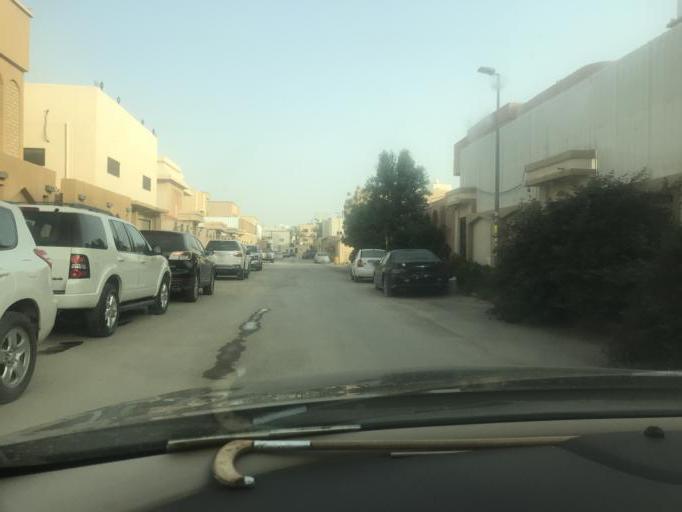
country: SA
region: Ar Riyad
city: Riyadh
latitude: 24.7444
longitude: 46.7708
